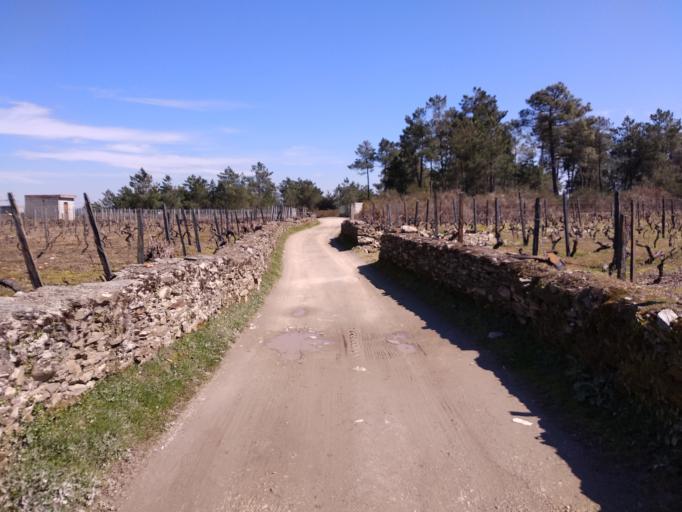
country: PT
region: Vila Real
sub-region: Sabrosa
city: Vilela
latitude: 41.1895
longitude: -7.6764
